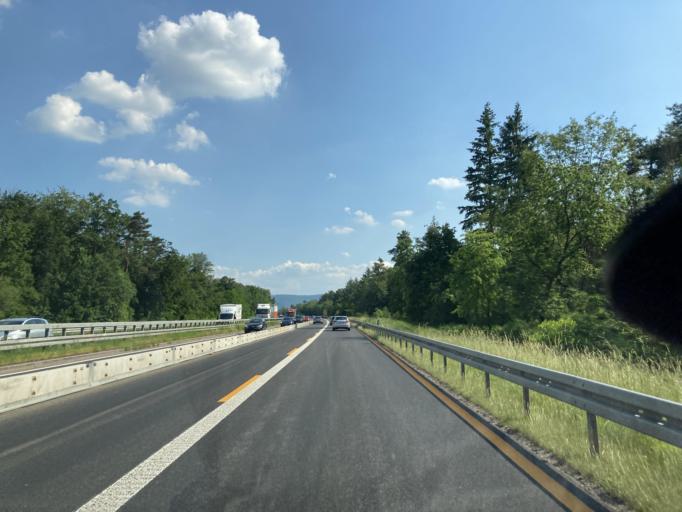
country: DE
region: Baden-Wuerttemberg
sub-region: Karlsruhe Region
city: Ettlingen
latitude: 48.9676
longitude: 8.3767
